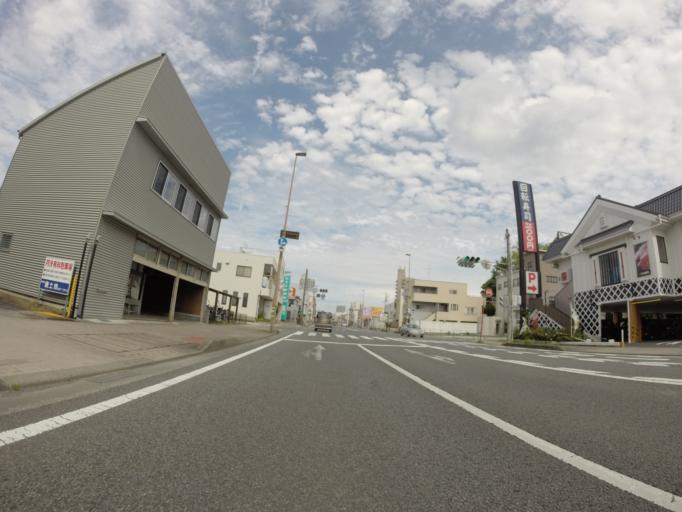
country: JP
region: Shizuoka
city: Shizuoka-shi
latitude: 35.0239
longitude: 138.4806
